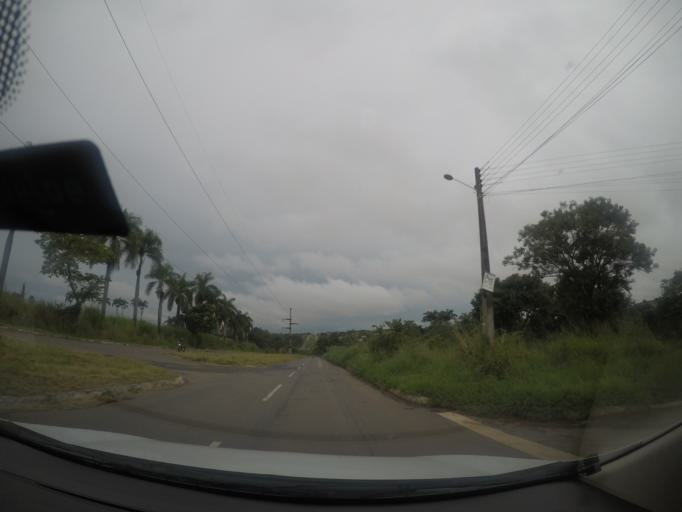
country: BR
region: Goias
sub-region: Aparecida De Goiania
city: Aparecida de Goiania
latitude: -16.7642
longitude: -49.3049
